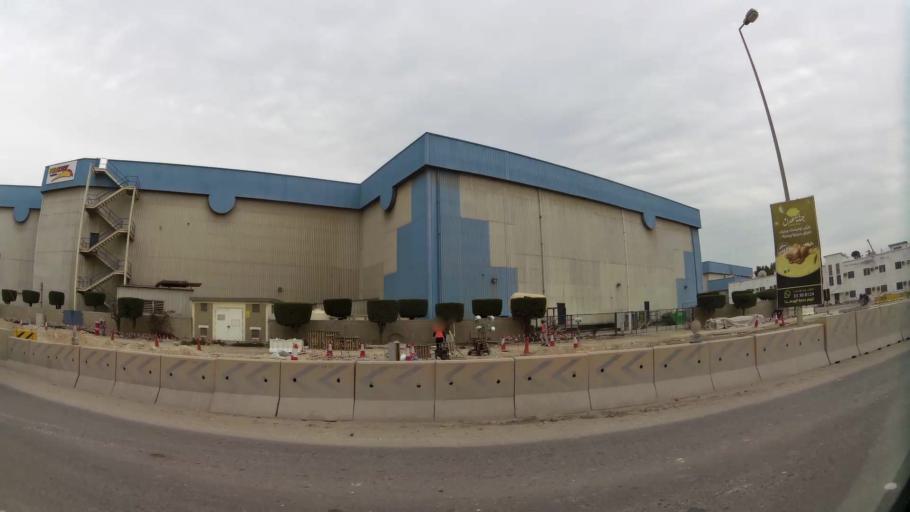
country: BH
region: Northern
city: Sitrah
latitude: 26.1293
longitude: 50.6017
